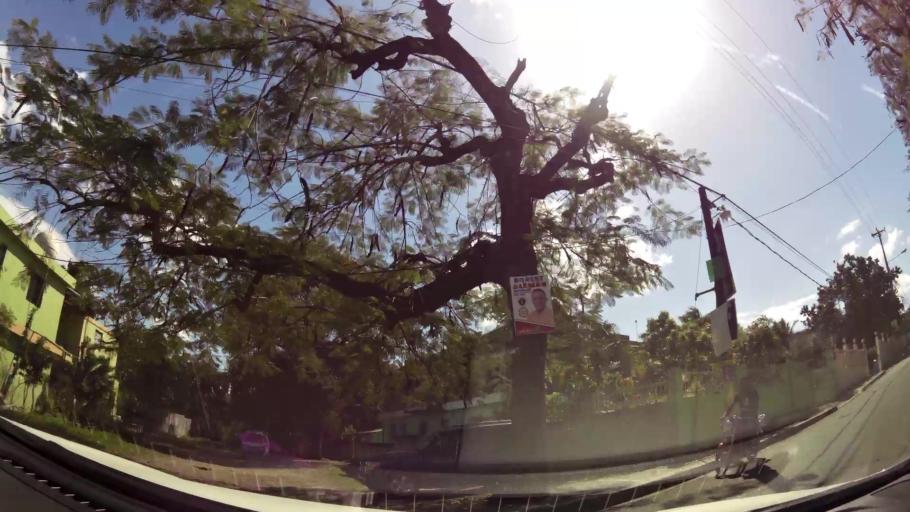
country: DO
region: San Cristobal
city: San Cristobal
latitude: 18.4285
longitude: -70.0829
